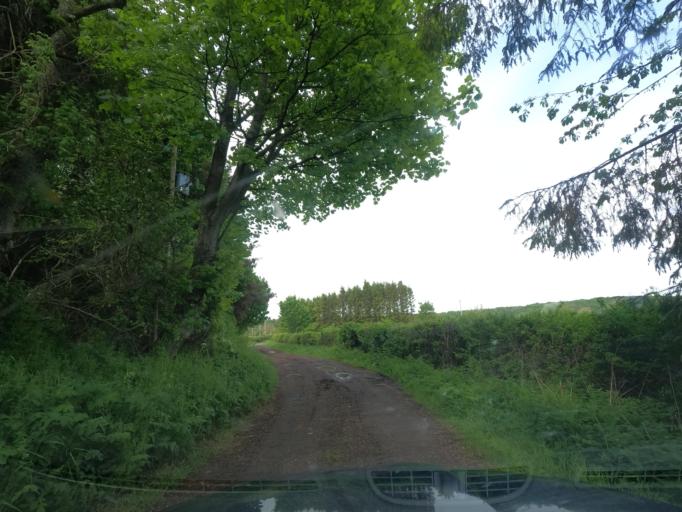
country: GB
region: England
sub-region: Northumberland
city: Kirknewton
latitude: 55.5689
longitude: -2.0995
